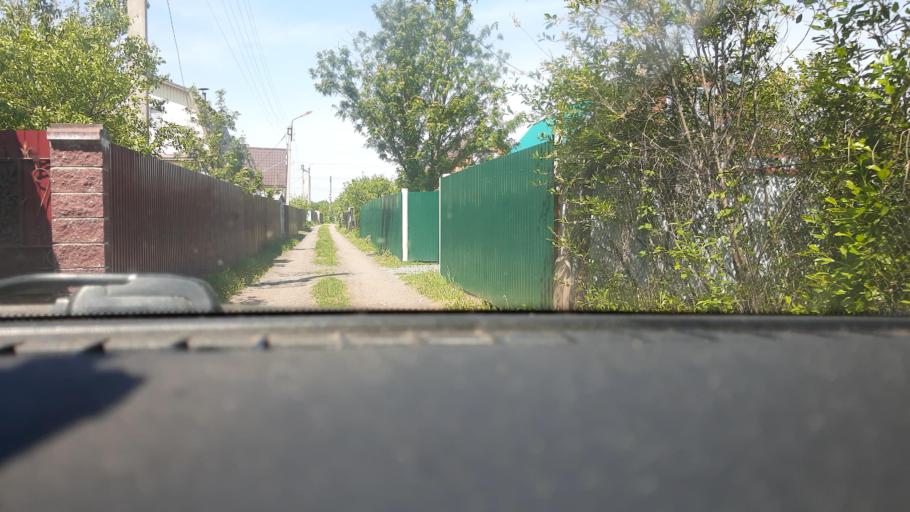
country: RU
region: Bashkortostan
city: Mikhaylovka
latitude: 54.7949
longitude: 55.8251
